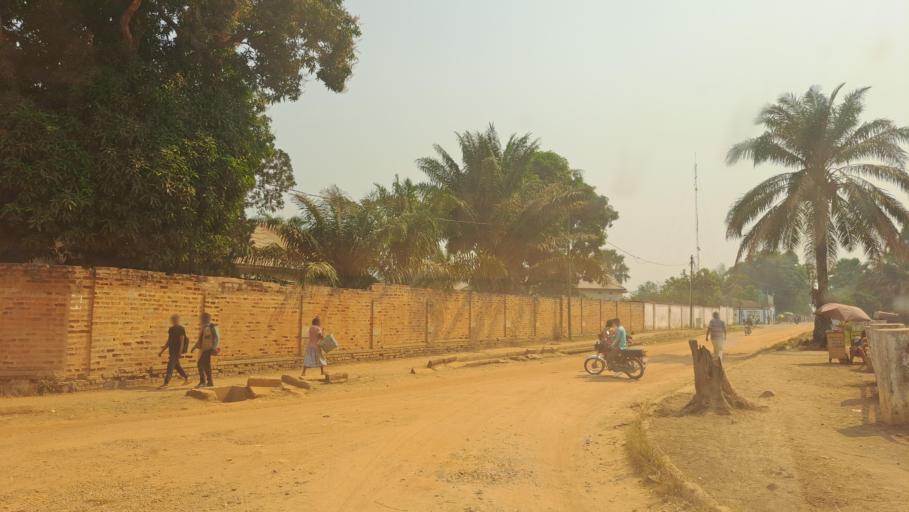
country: CD
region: Kasai-Occidental
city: Kananga
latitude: -5.9027
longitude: 22.4059
